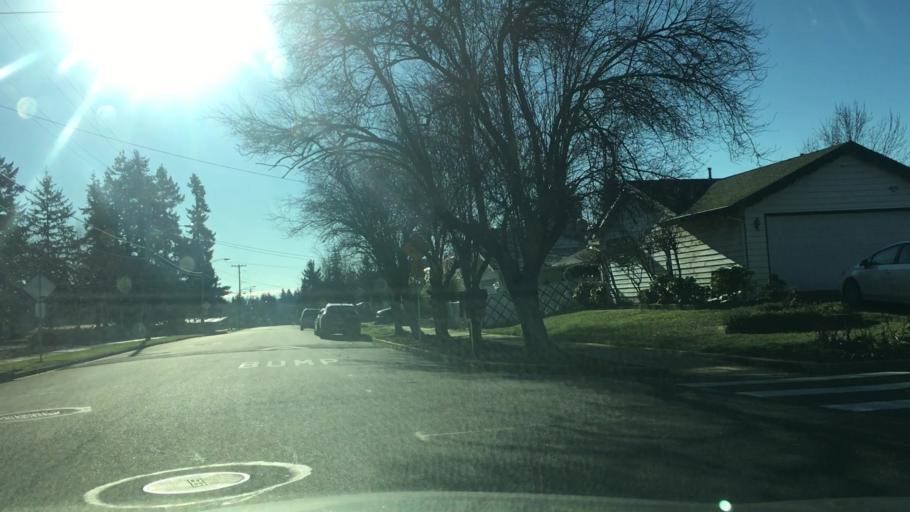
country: US
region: Washington
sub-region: King County
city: Lakeland North
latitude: 47.3629
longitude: -122.2840
